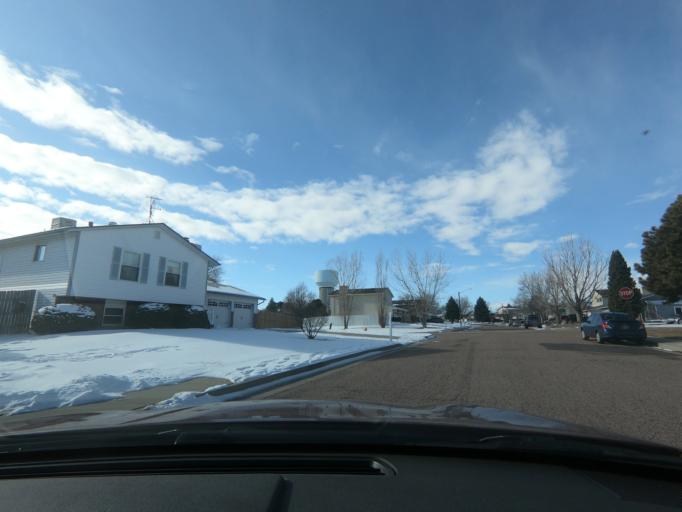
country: US
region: Colorado
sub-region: El Paso County
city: Security-Widefield
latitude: 38.7325
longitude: -104.6862
